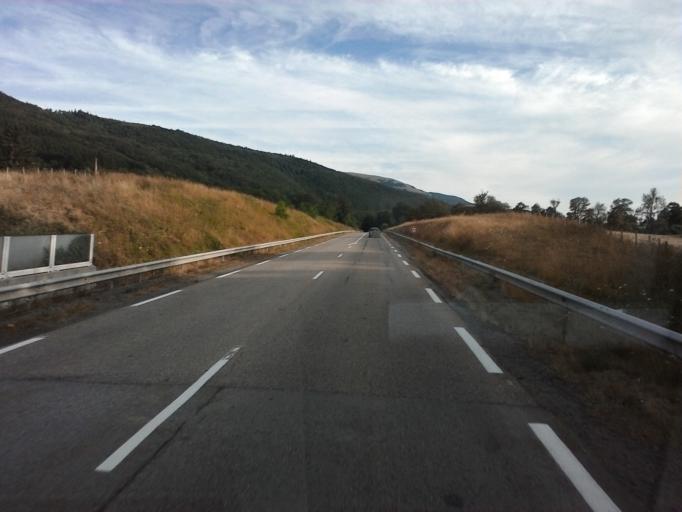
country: FR
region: Rhone-Alpes
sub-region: Departement de l'Isere
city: Pierre-Chatel
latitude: 44.9645
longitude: 5.7772
